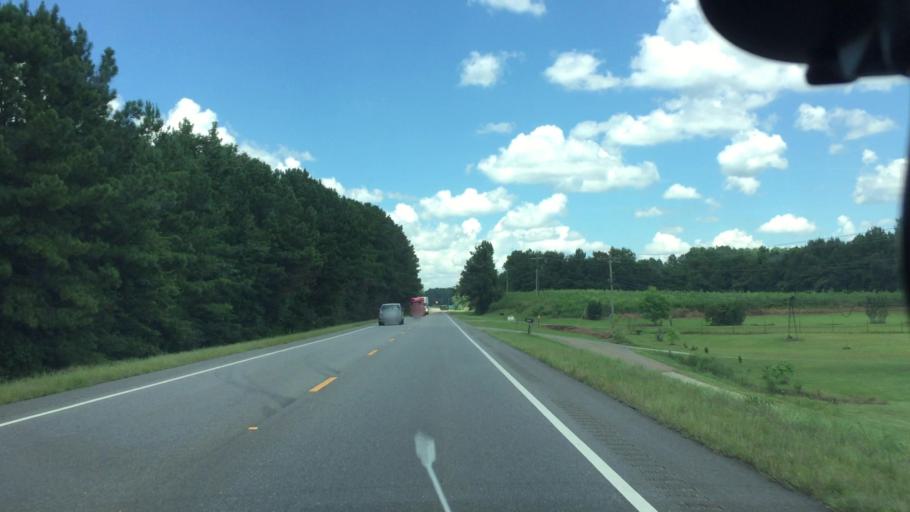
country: US
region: Alabama
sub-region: Coffee County
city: New Brockton
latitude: 31.5378
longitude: -85.9184
